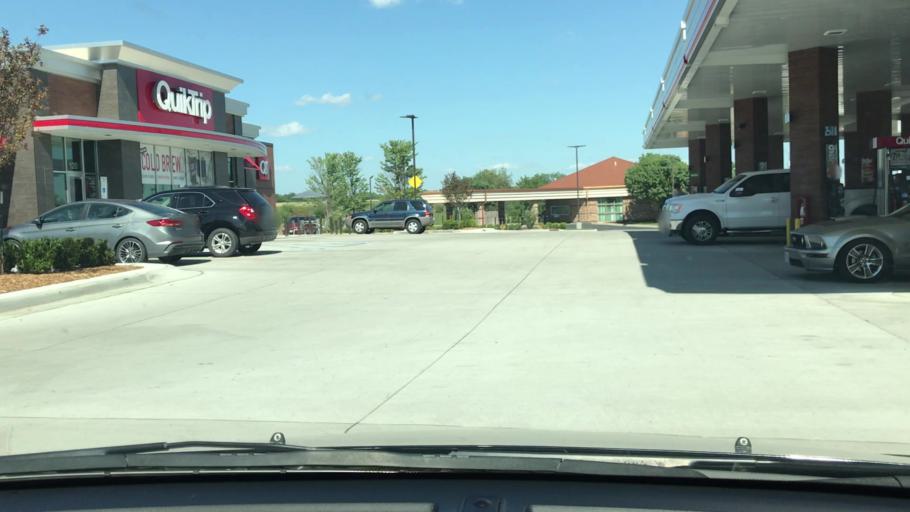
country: US
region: Missouri
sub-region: Cass County
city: Lake Winnebago
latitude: 38.8532
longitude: -94.3791
